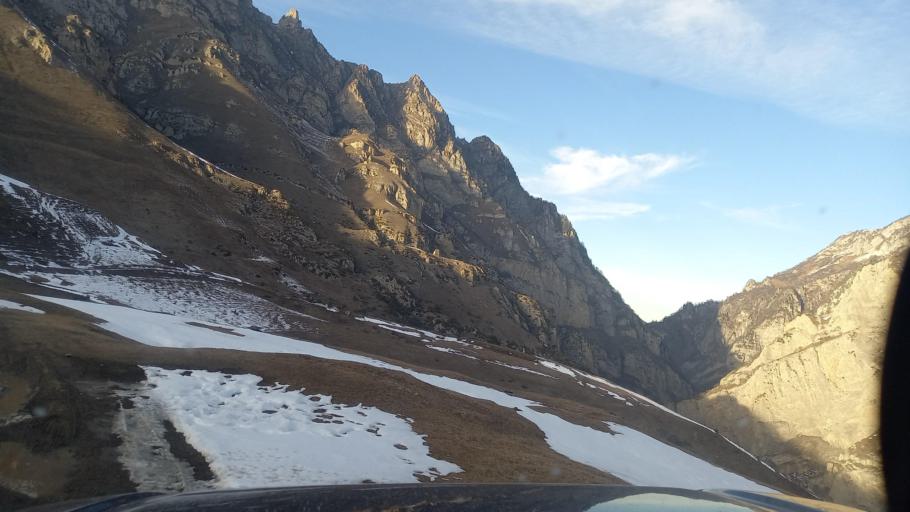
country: RU
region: Ingushetiya
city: Dzhayrakh
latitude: 42.8559
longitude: 44.5156
